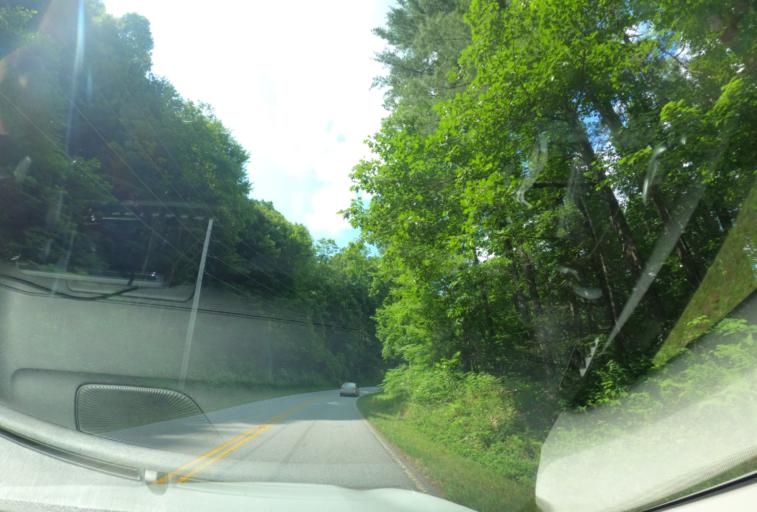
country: US
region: North Carolina
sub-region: Jackson County
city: Cullowhee
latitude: 35.0795
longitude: -82.9932
